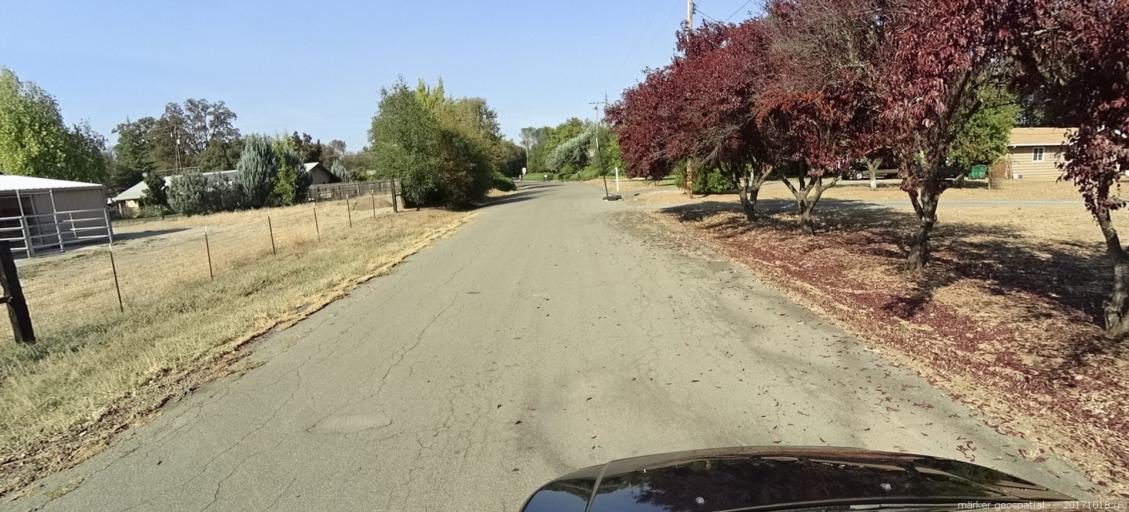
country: US
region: California
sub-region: Shasta County
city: Palo Cedro
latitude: 40.5716
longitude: -122.2285
